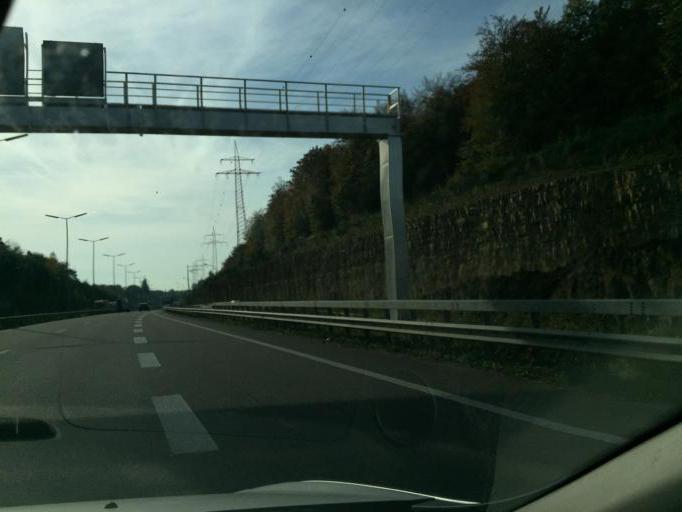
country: LU
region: Luxembourg
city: Helmsange
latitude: 49.6517
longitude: 6.1853
